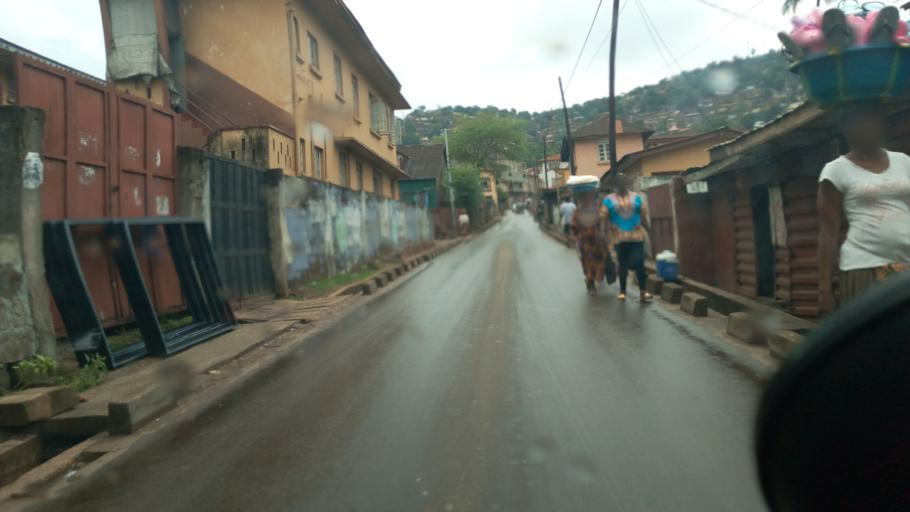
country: SL
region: Western Area
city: Freetown
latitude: 8.4770
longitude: -13.2340
